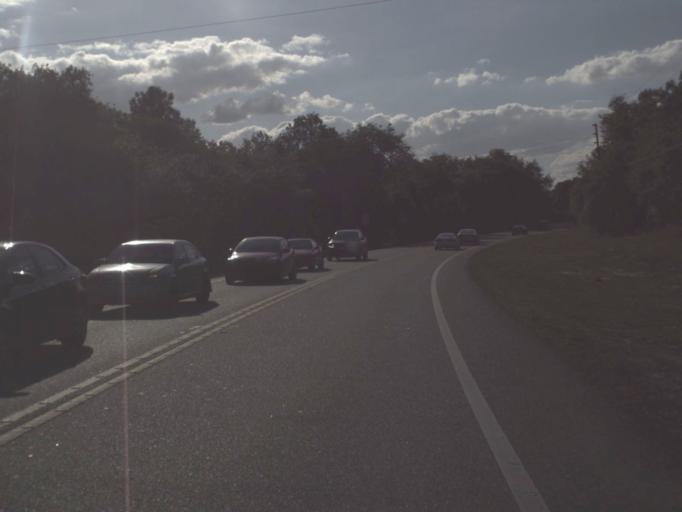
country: US
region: Florida
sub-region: Lake County
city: Mount Plymouth
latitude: 28.8112
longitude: -81.4637
